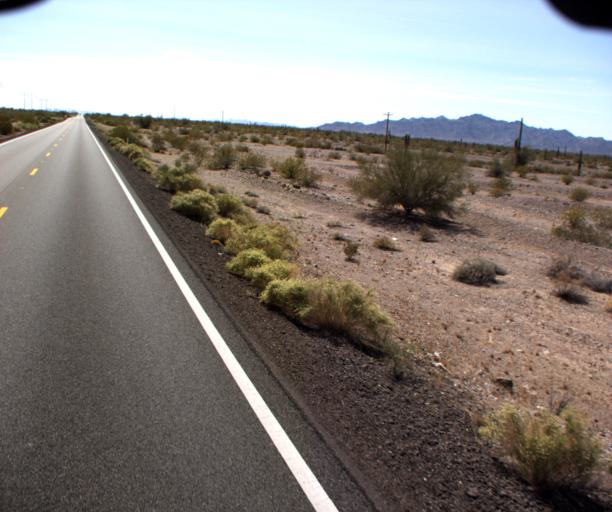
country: US
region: Arizona
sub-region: La Paz County
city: Quartzsite
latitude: 33.5990
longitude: -114.2171
